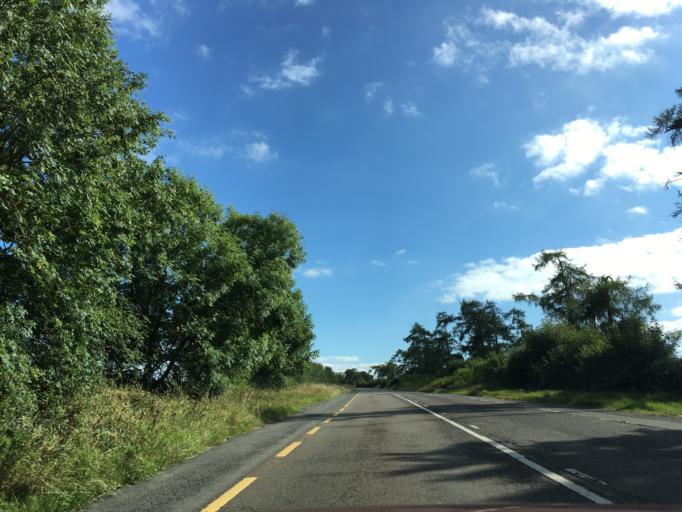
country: IE
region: Munster
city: Cashel
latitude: 52.4823
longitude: -7.8918
